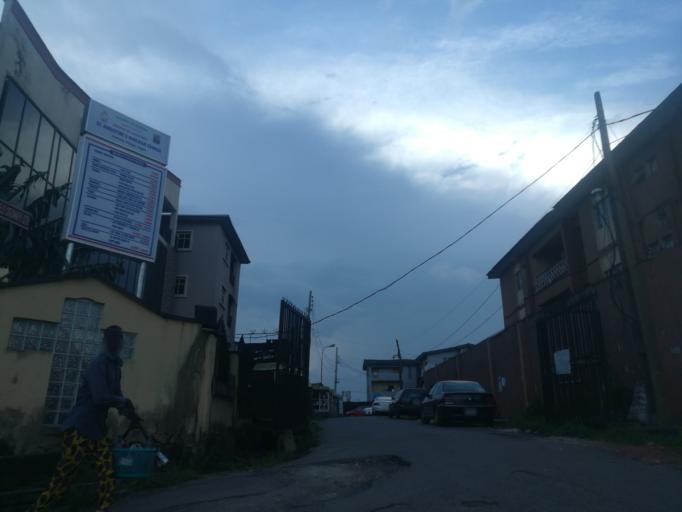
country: NG
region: Lagos
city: Somolu
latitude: 6.5593
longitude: 3.3714
